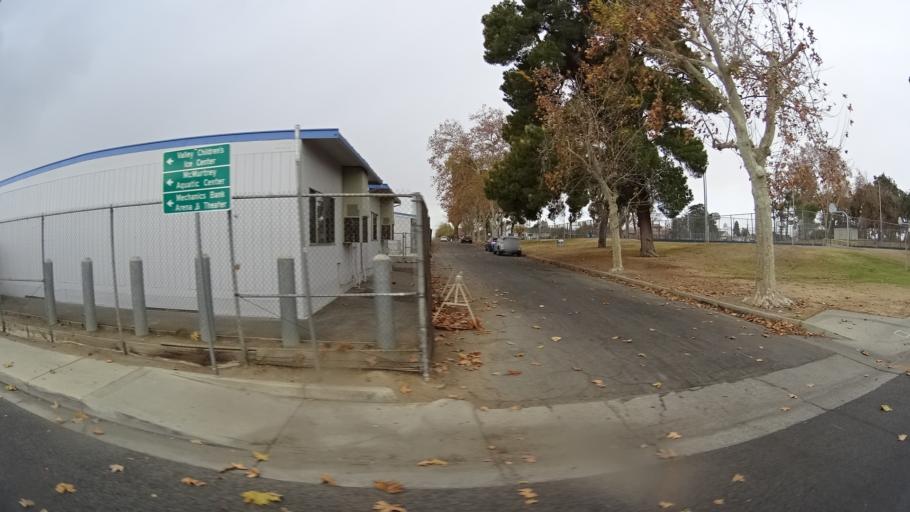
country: US
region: California
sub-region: Kern County
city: Bakersfield
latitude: 35.3877
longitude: -118.9857
